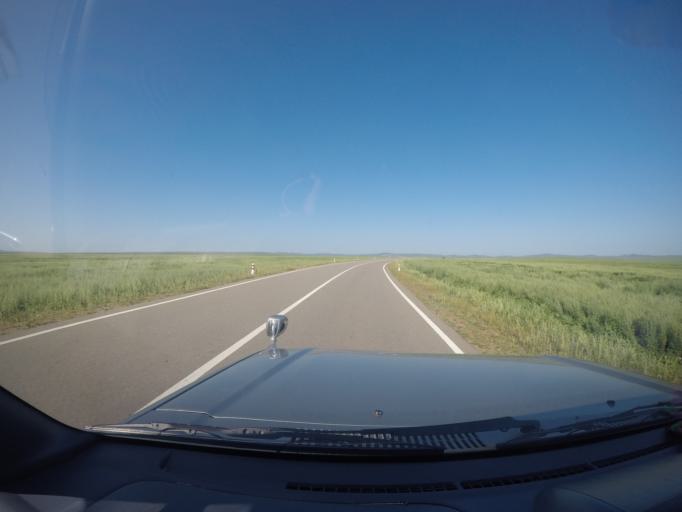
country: MN
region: Suhbaatar
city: Hanhohiy
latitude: 47.5663
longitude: 112.2756
